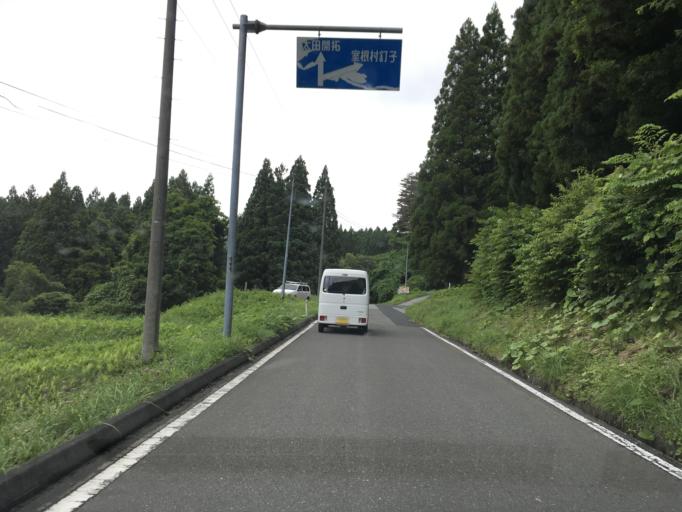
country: JP
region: Iwate
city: Ofunato
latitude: 38.8848
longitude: 141.4732
